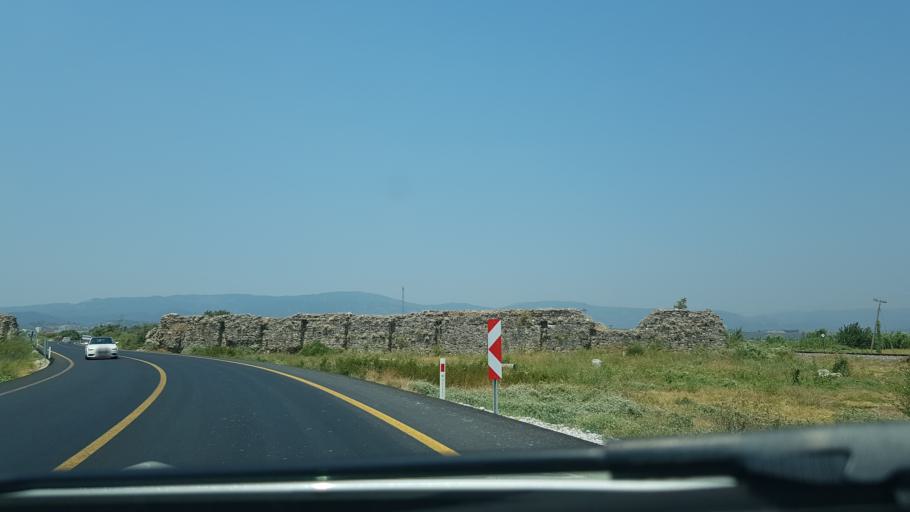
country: TR
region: Aydin
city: Ortaklar
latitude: 37.8535
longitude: 27.5283
